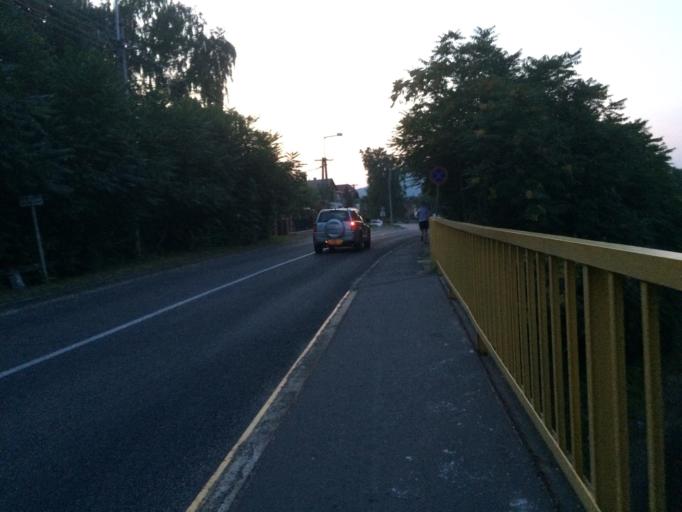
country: HU
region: Veszprem
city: Badacsonytomaj
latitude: 46.8016
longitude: 17.5165
